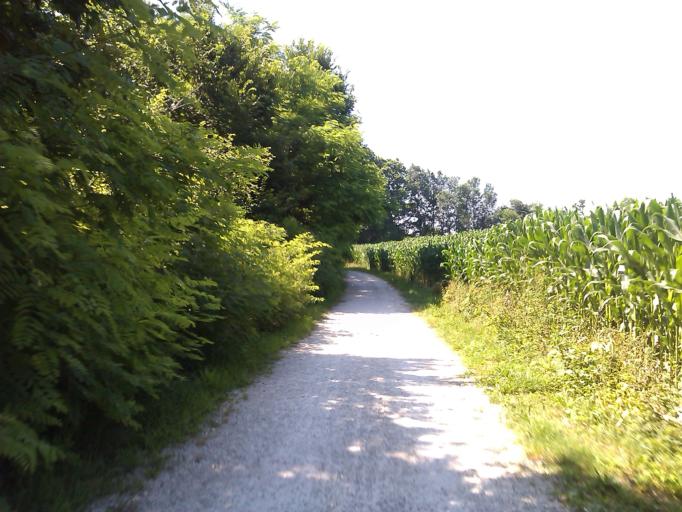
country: IT
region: Veneto
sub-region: Provincia di Treviso
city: Ramon
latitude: 45.7084
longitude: 11.8803
